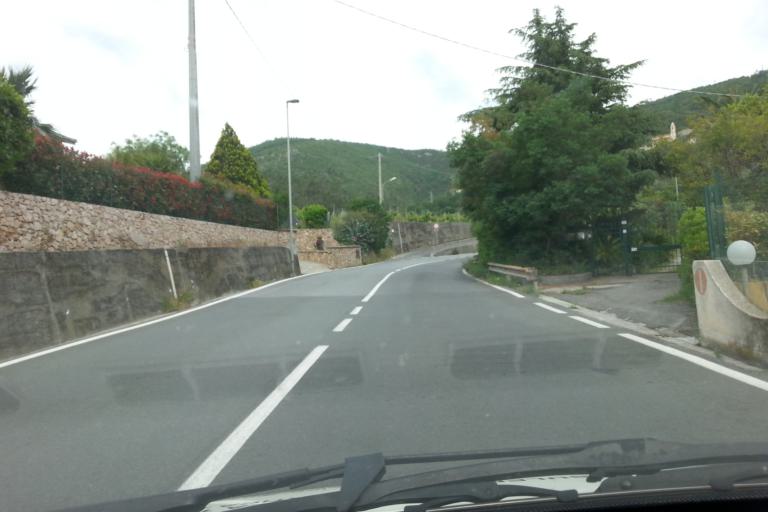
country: IT
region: Liguria
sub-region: Provincia di Savona
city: Pietra Ligure
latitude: 44.1490
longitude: 8.2681
